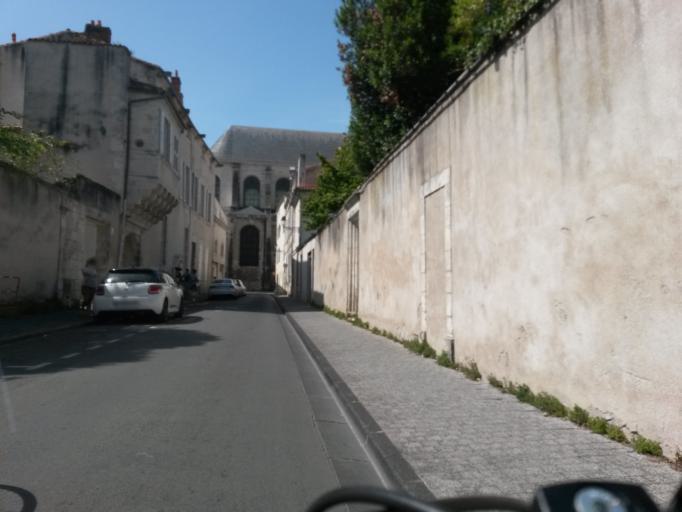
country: FR
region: Poitou-Charentes
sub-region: Departement de la Charente-Maritime
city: La Rochelle
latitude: 46.1611
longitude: -1.1520
